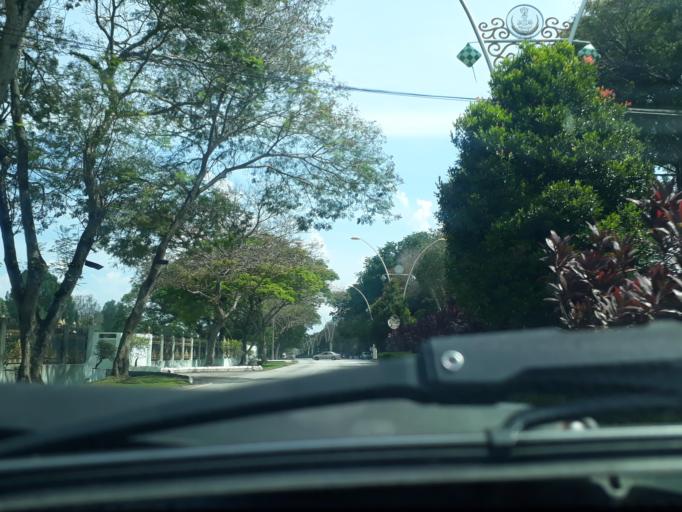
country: MY
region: Perak
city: Ipoh
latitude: 4.5852
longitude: 101.1103
